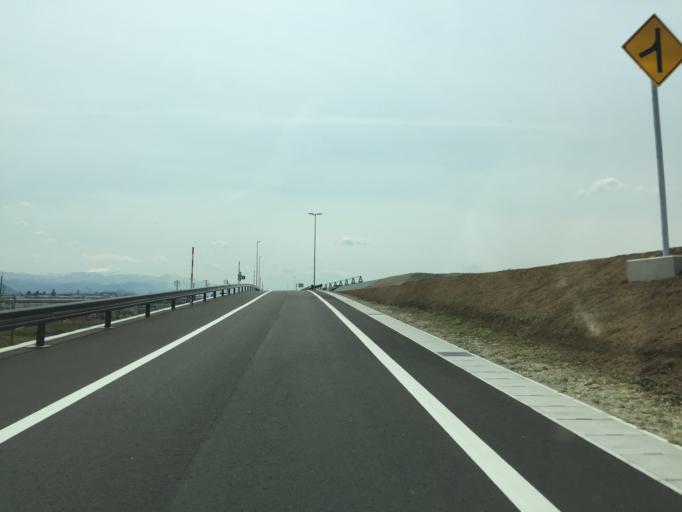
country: JP
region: Yamagata
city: Higashine
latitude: 38.4465
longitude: 140.3541
